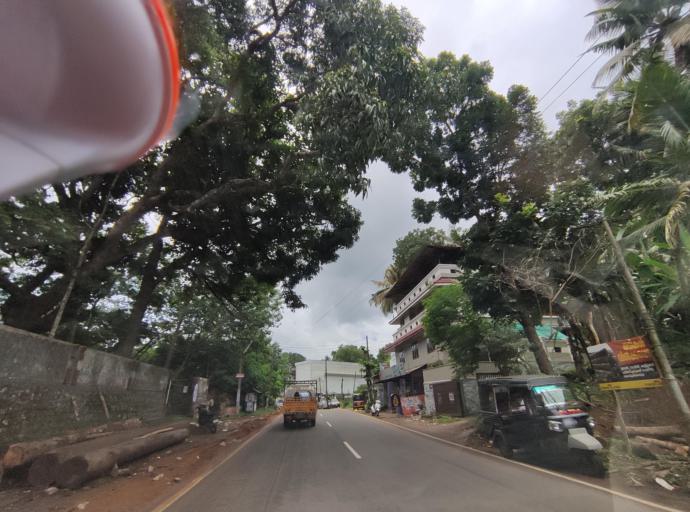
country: IN
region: Kerala
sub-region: Thiruvananthapuram
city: Nedumangad
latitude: 8.5838
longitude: 76.9469
